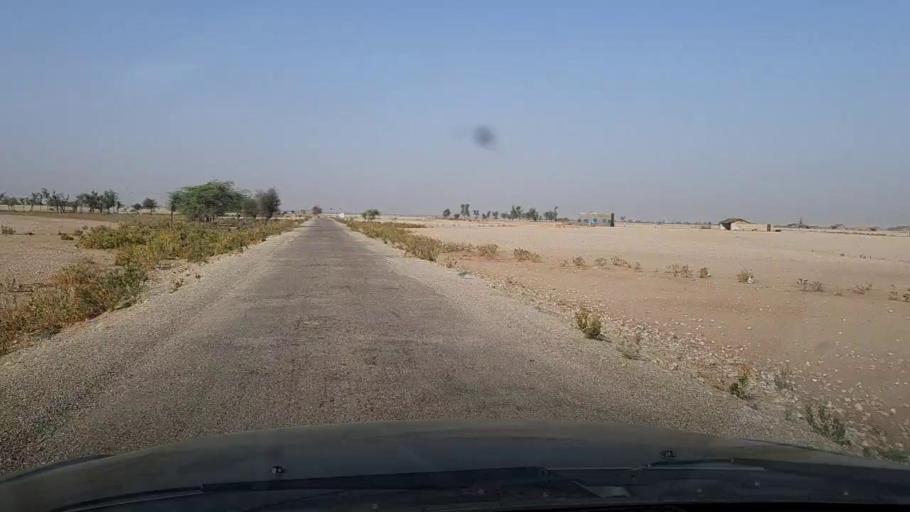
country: PK
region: Sindh
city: Sann
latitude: 26.0014
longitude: 68.0789
